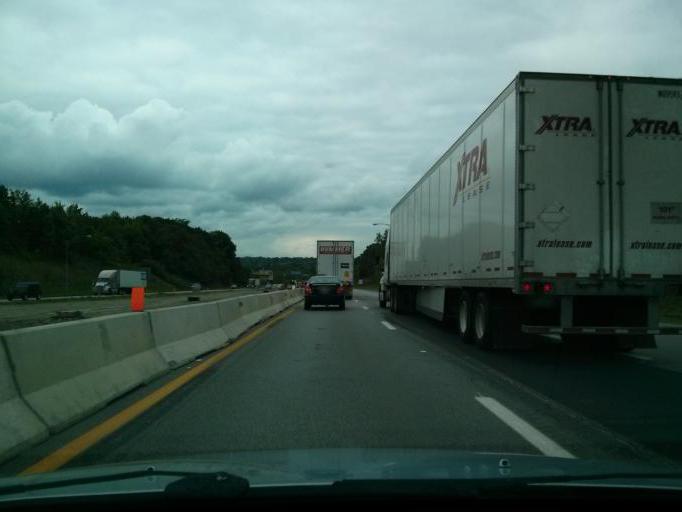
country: US
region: Ohio
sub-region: Trumbull County
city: Girard
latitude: 41.1440
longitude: -80.7158
